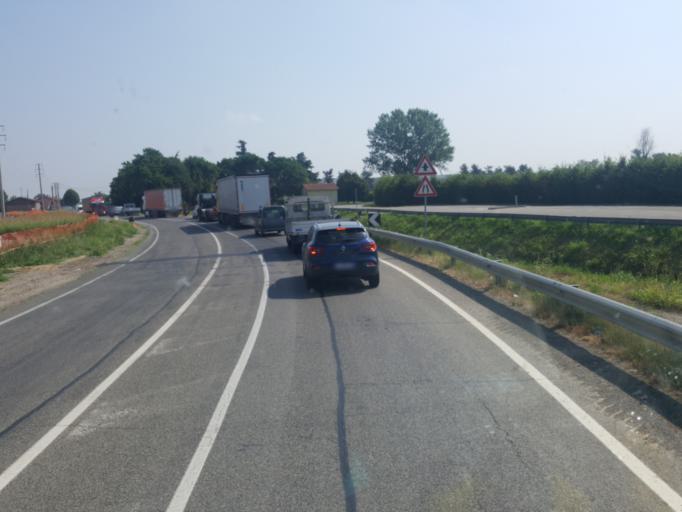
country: IT
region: Emilia-Romagna
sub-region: Provincia di Bologna
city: Imola
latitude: 44.3871
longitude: 11.7334
